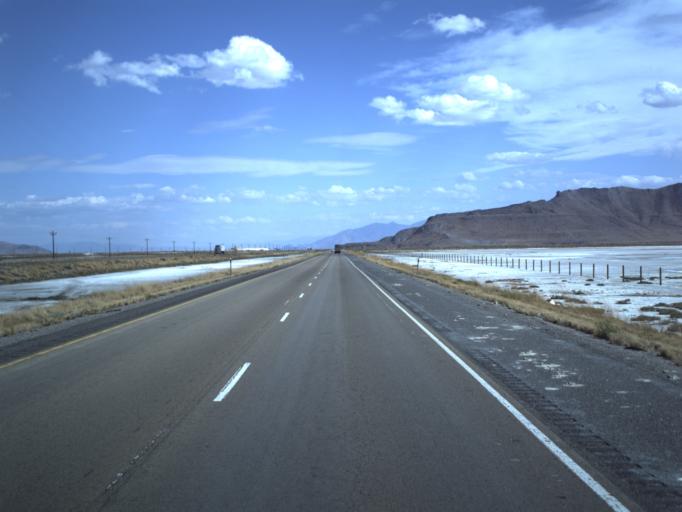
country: US
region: Utah
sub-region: Tooele County
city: Grantsville
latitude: 40.7512
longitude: -112.7082
